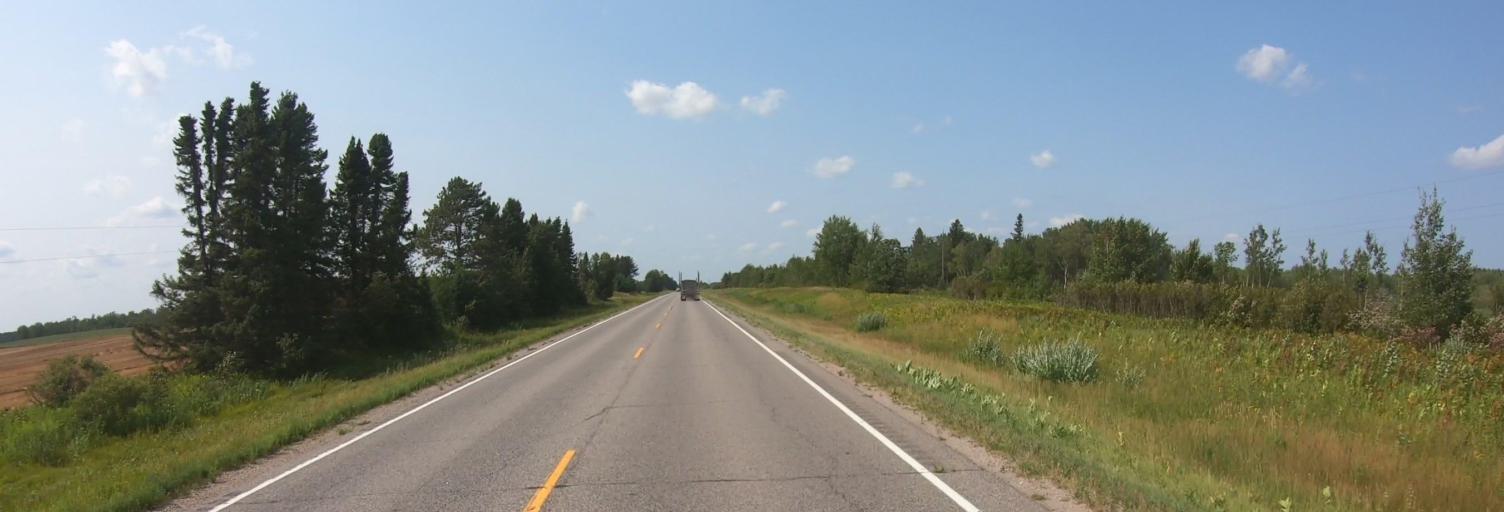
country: US
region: Minnesota
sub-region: Roseau County
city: Warroad
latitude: 48.8232
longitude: -95.1483
